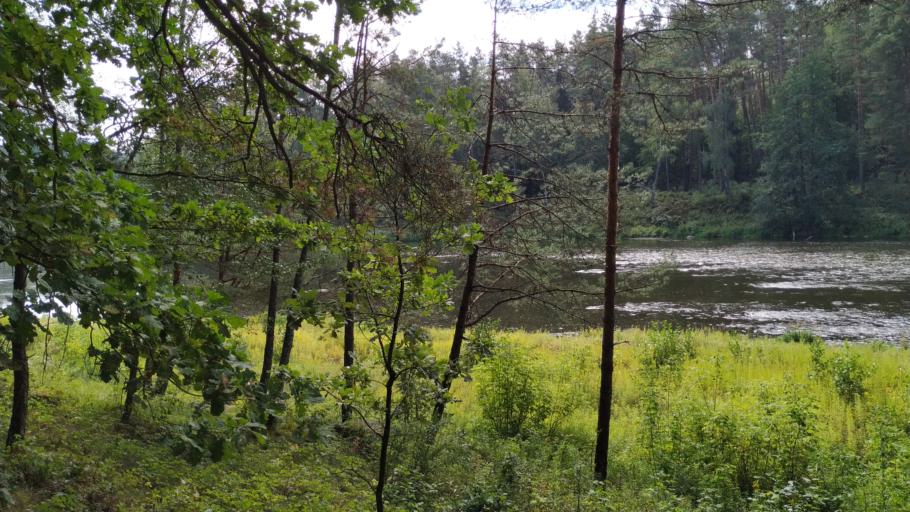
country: LT
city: Grigiskes
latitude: 54.8067
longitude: 24.9677
